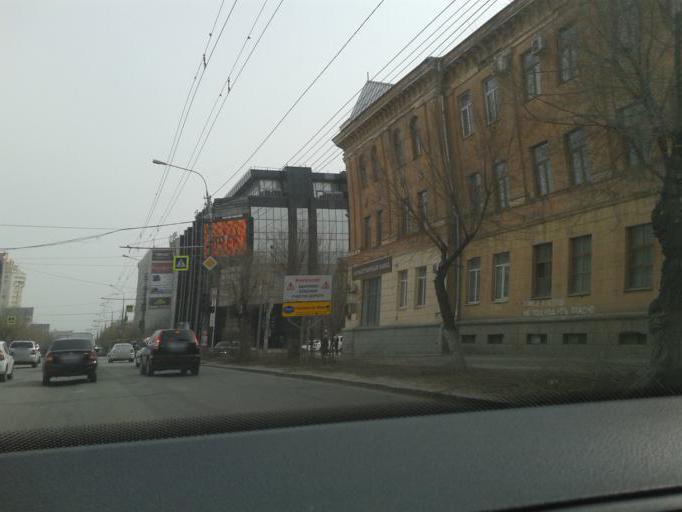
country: RU
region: Volgograd
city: Volgograd
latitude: 48.7196
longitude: 44.5057
